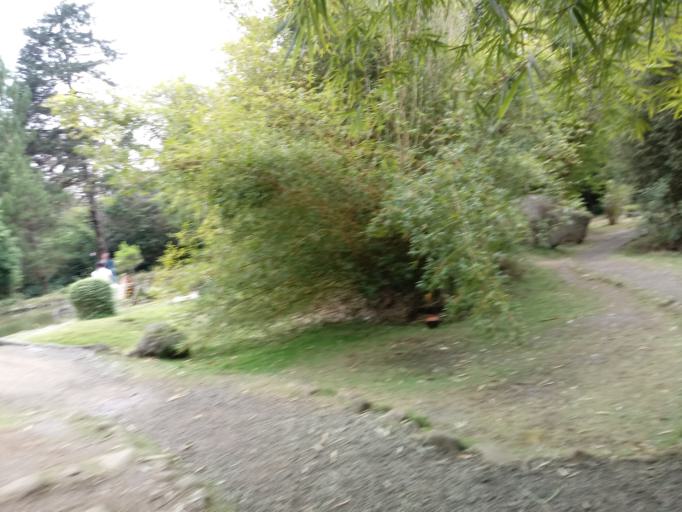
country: CR
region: Cartago
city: Paraiso
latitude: 9.8404
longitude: -83.8894
